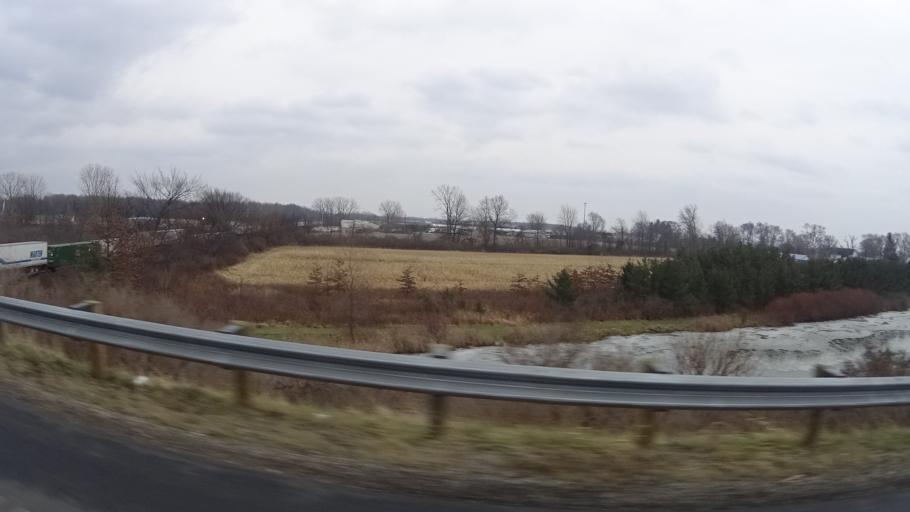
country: US
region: Ohio
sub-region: Lorain County
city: Elyria
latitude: 41.3783
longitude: -82.1546
